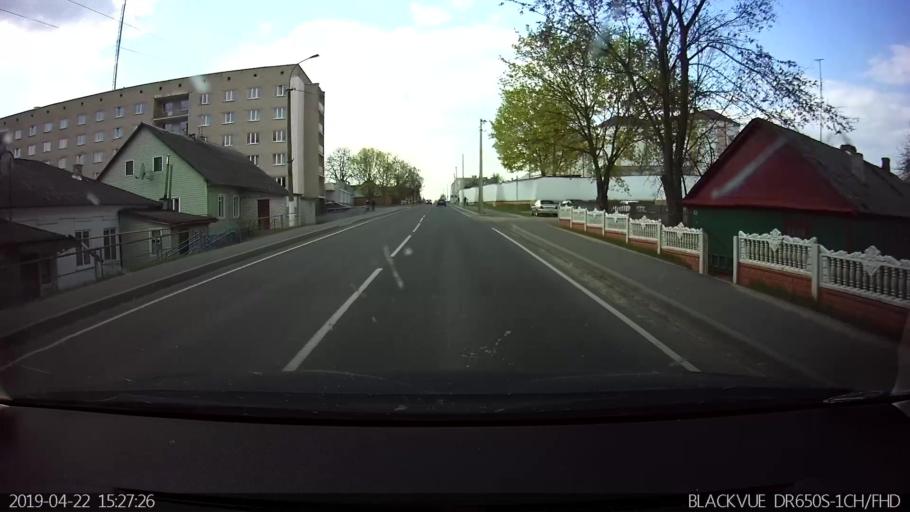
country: BY
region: Brest
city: Vysokaye
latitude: 52.3707
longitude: 23.3715
